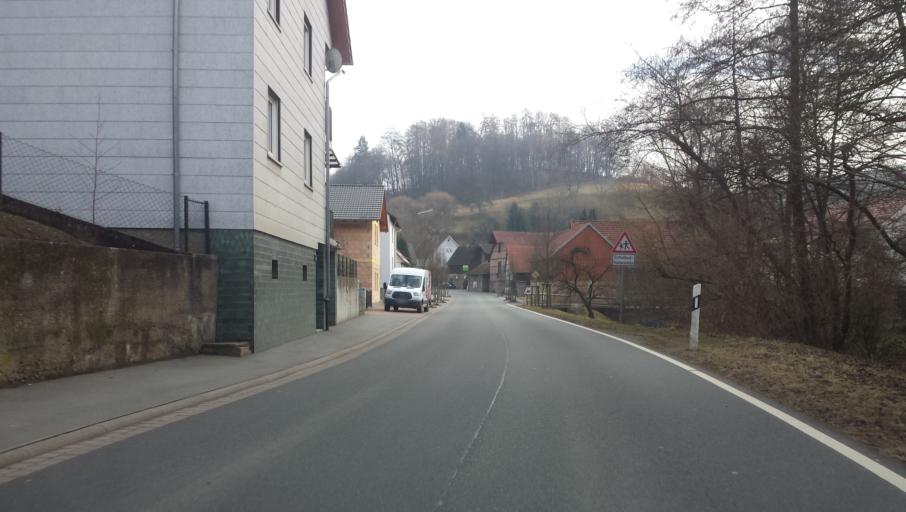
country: DE
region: Hesse
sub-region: Regierungsbezirk Darmstadt
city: Frankisch-Crumbach
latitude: 49.7254
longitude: 8.8997
